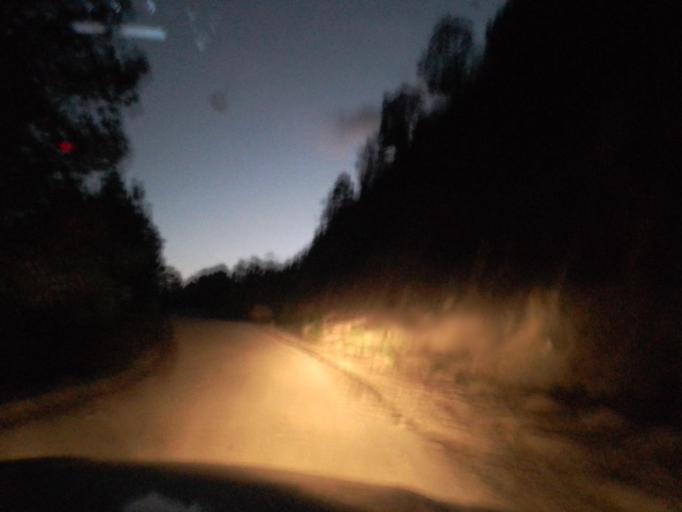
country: GT
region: San Marcos
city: Tacana
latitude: 15.2360
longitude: -92.1994
